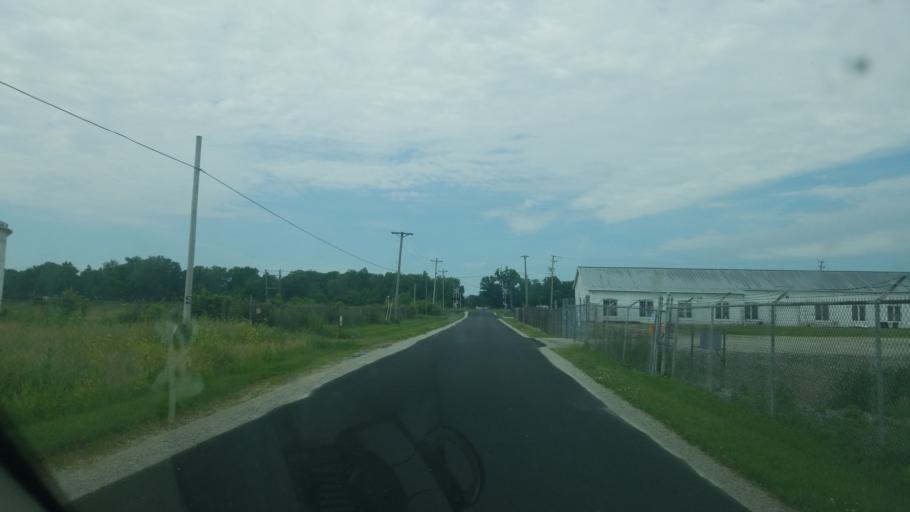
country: US
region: Ohio
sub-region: Wood County
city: North Baltimore
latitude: 41.2220
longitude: -83.6434
